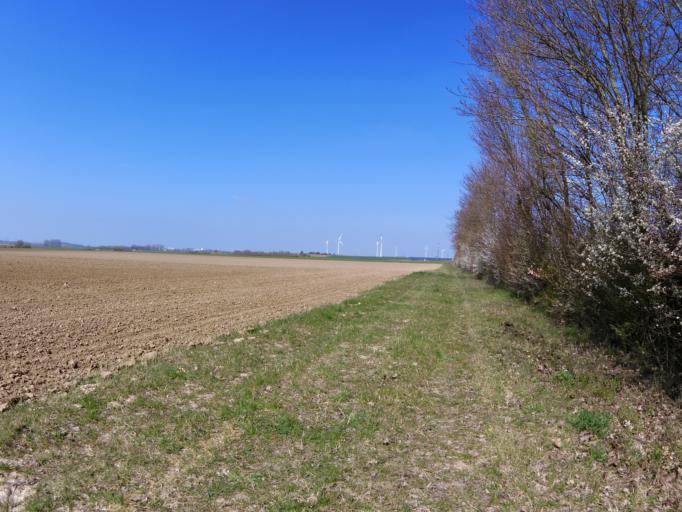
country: DE
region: Bavaria
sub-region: Regierungsbezirk Unterfranken
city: Sulzfeld am Main
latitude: 49.7277
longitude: 10.1030
